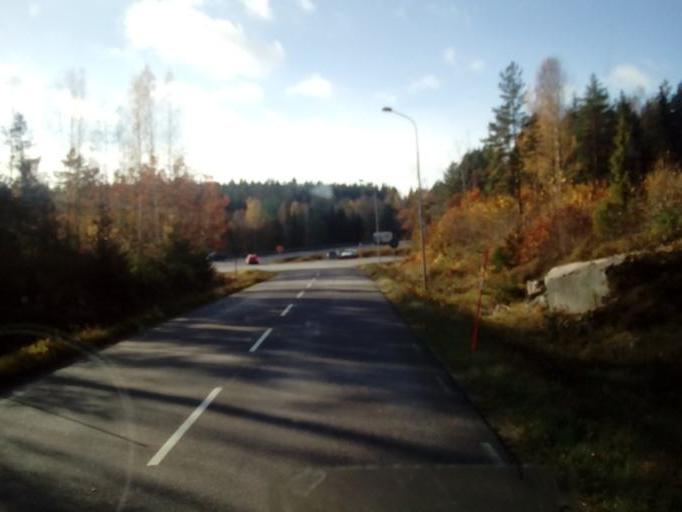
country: SE
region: Kalmar
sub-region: Vimmerby Kommun
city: Vimmerby
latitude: 57.7185
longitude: 16.0675
